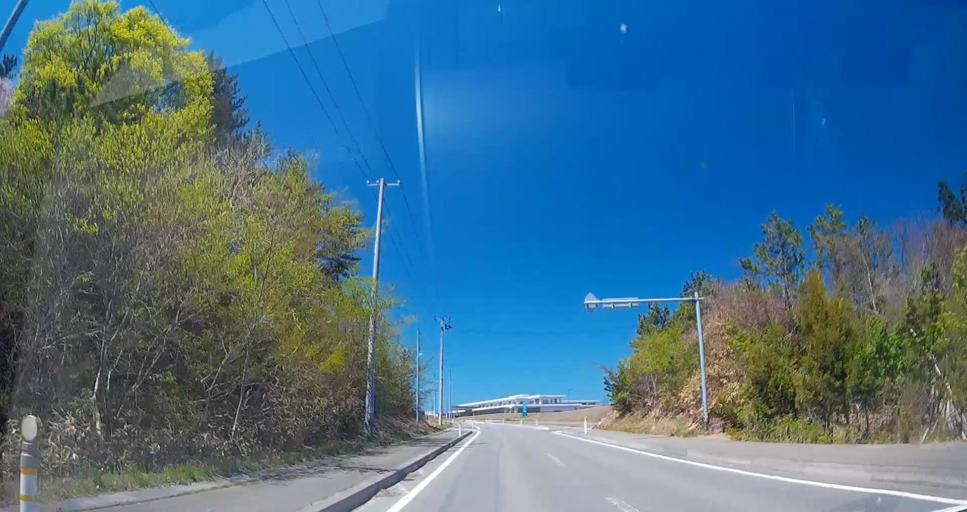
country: JP
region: Aomori
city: Misawa
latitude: 40.9690
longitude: 141.3731
